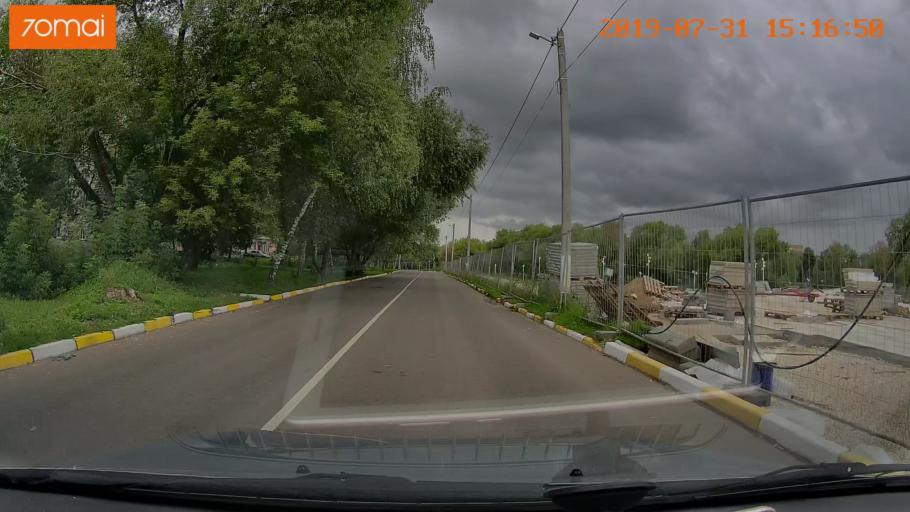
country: RU
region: Moskovskaya
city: Voskresensk
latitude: 55.3179
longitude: 38.6588
